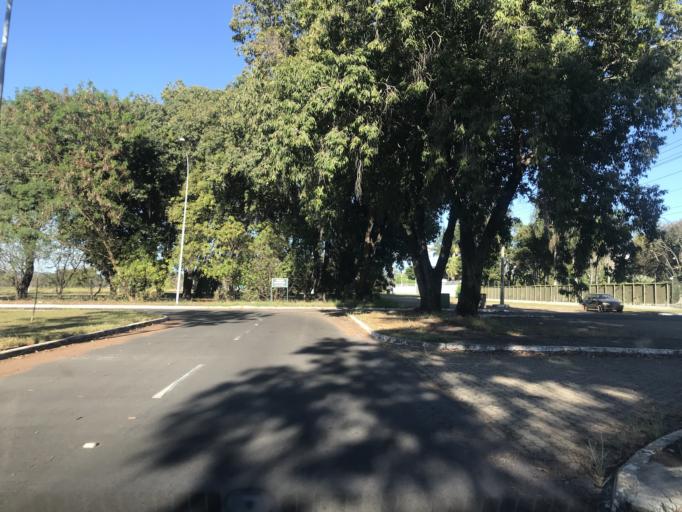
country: BR
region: Federal District
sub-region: Brasilia
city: Brasilia
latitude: -15.8246
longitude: -47.8919
